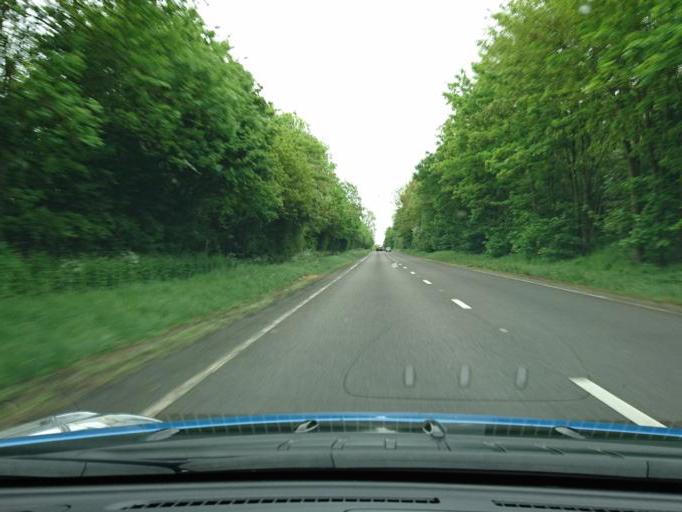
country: GB
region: England
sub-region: Oxfordshire
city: Wheatley
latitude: 51.7609
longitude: -1.1595
